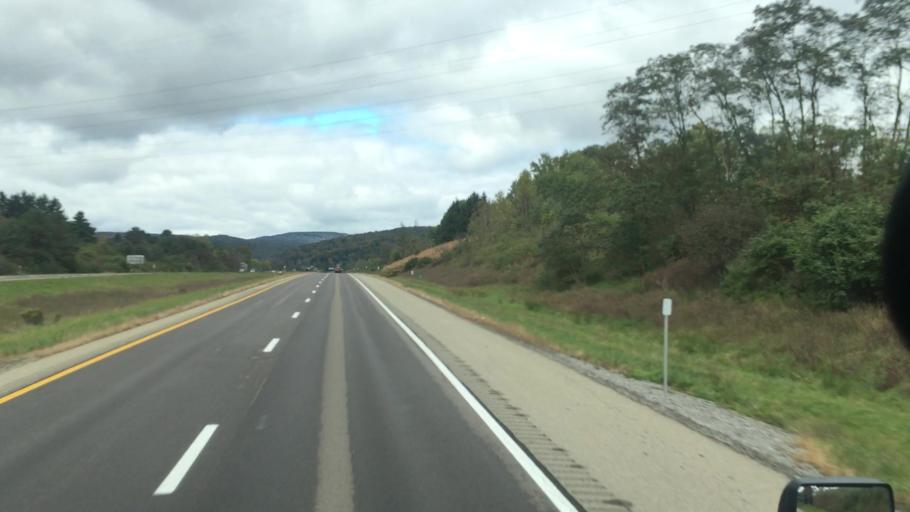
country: US
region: New York
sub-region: Cattaraugus County
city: Saint Bonaventure
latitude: 42.0929
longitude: -78.4718
